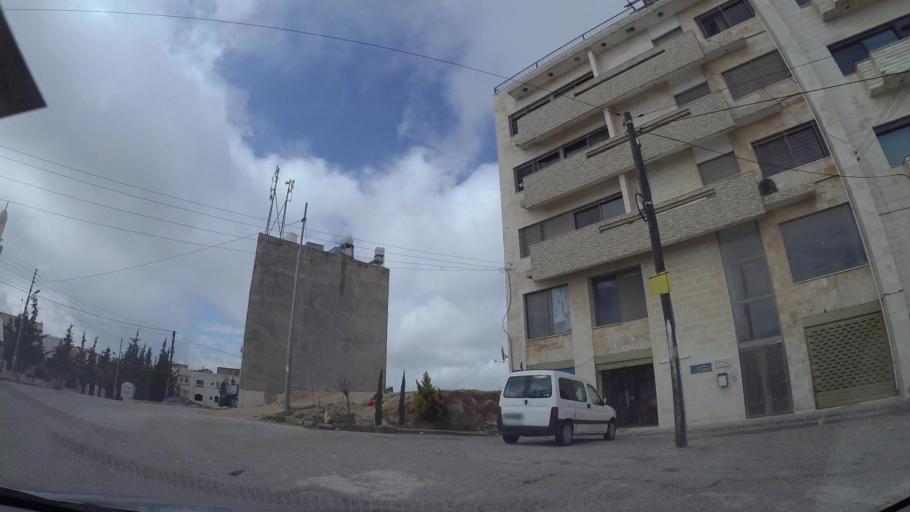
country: JO
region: Amman
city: Al Jubayhah
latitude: 32.0664
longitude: 35.8805
